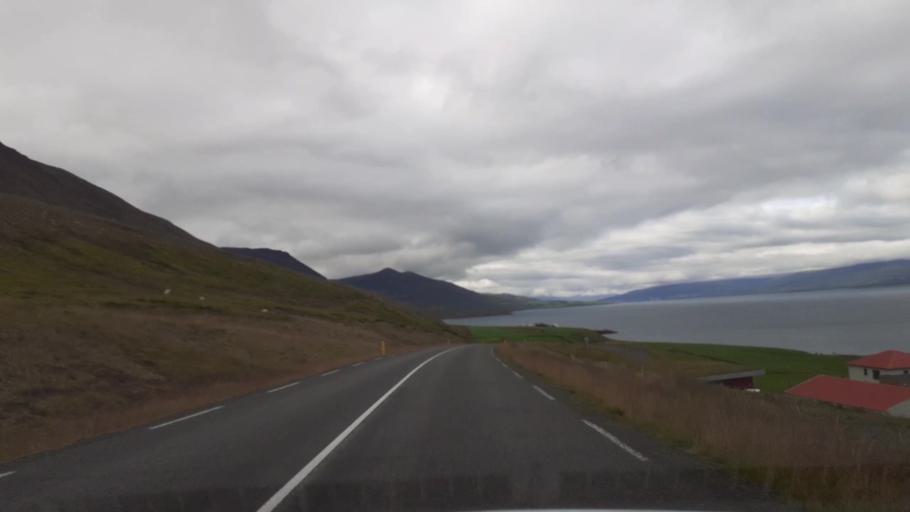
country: IS
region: Northeast
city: Akureyri
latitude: 65.8711
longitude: -18.0763
